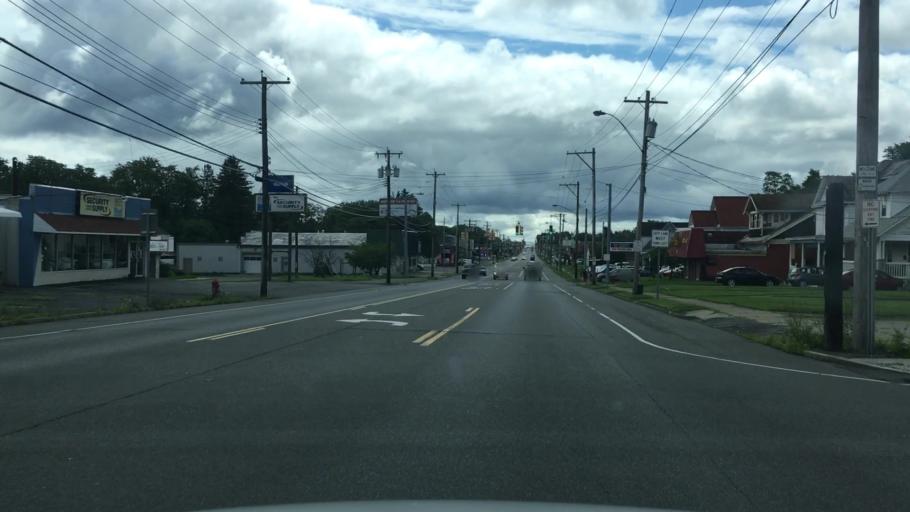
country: US
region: New York
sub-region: Schenectady County
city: Schenectady
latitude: 42.7839
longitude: -73.9080
